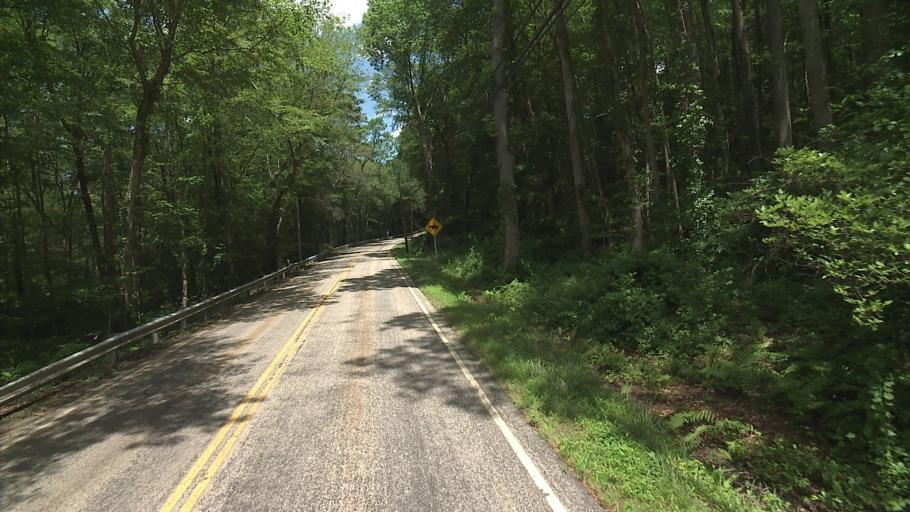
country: US
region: Connecticut
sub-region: Middlesex County
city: Moodus
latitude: 41.4766
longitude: -72.3796
